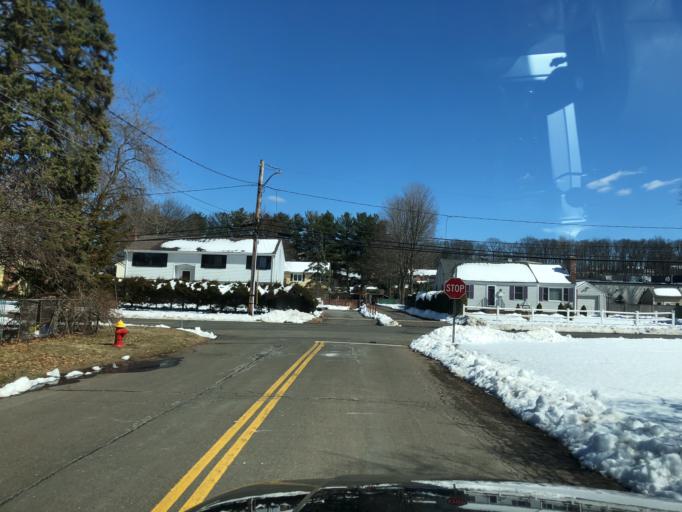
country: US
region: Connecticut
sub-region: Hartford County
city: Newington
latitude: 41.6868
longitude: -72.7109
